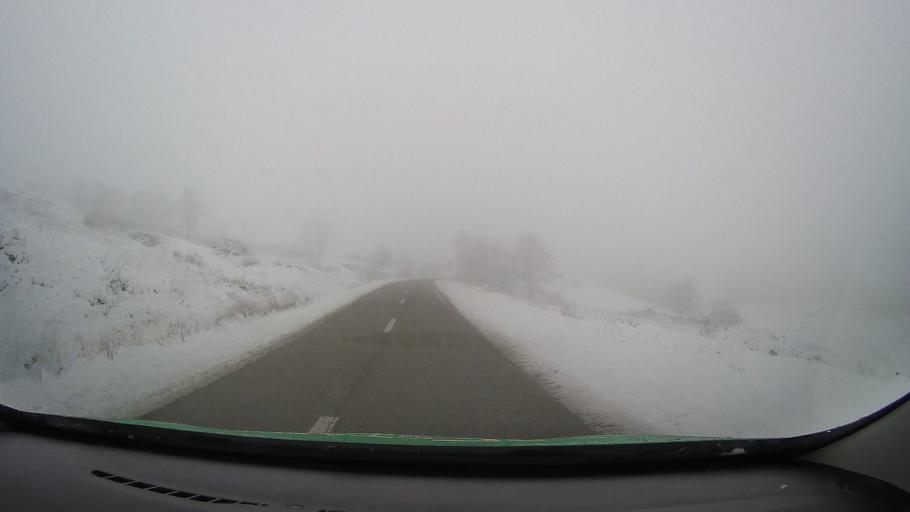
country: RO
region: Hunedoara
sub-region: Comuna Unirea
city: Unirea
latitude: 45.6647
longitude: 22.9145
